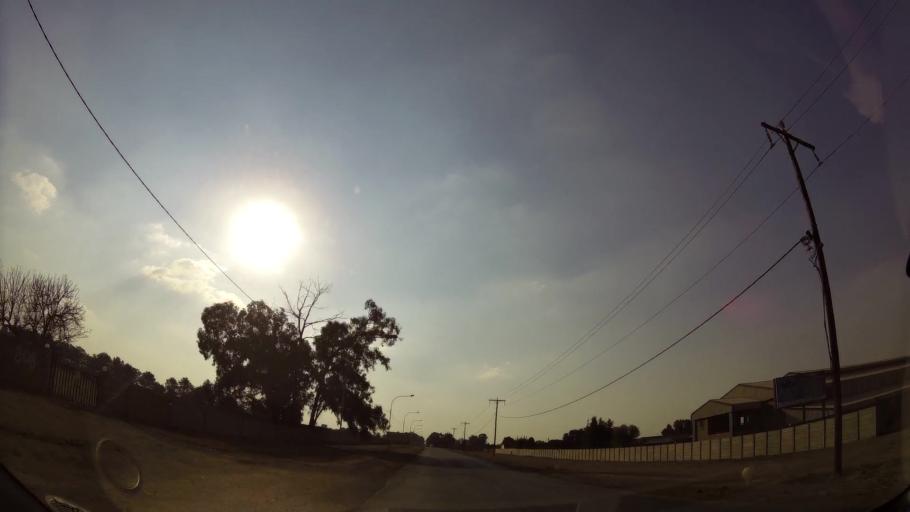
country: ZA
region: Gauteng
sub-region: Ekurhuleni Metropolitan Municipality
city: Benoni
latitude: -26.1179
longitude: 28.3898
